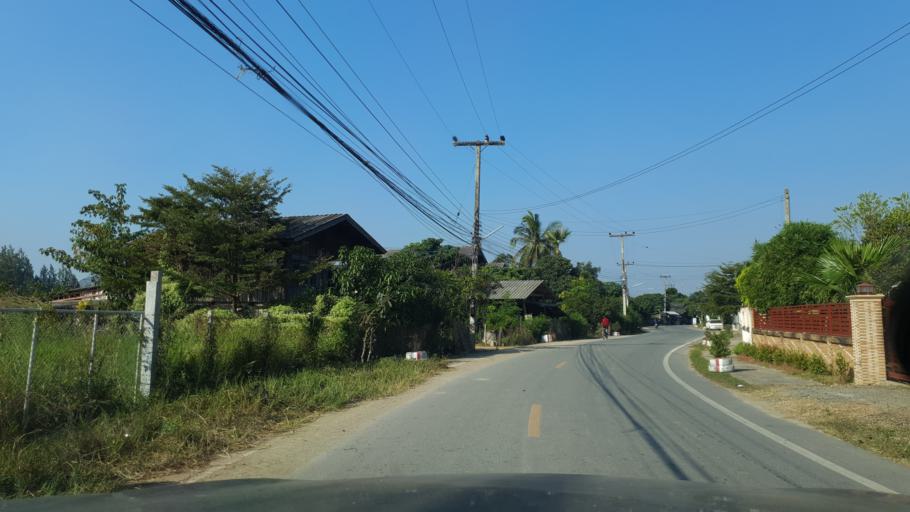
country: TH
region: Lamphun
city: Ban Thi
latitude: 18.6844
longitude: 99.1097
